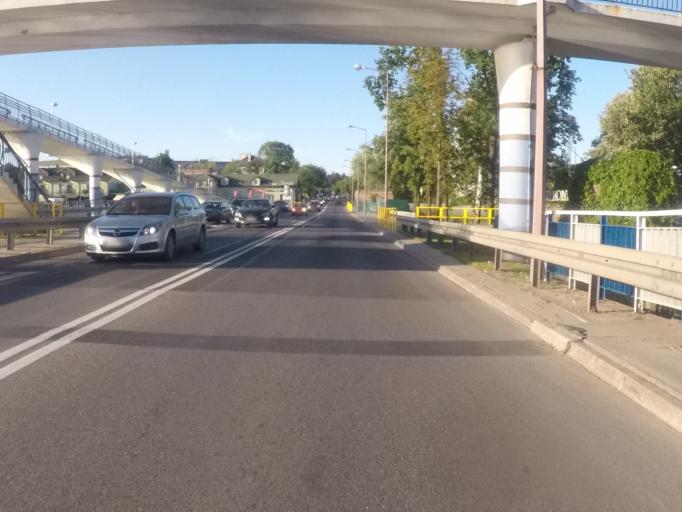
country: PL
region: Podlasie
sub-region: Powiat augustowski
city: Augustow
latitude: 53.8434
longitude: 22.9950
